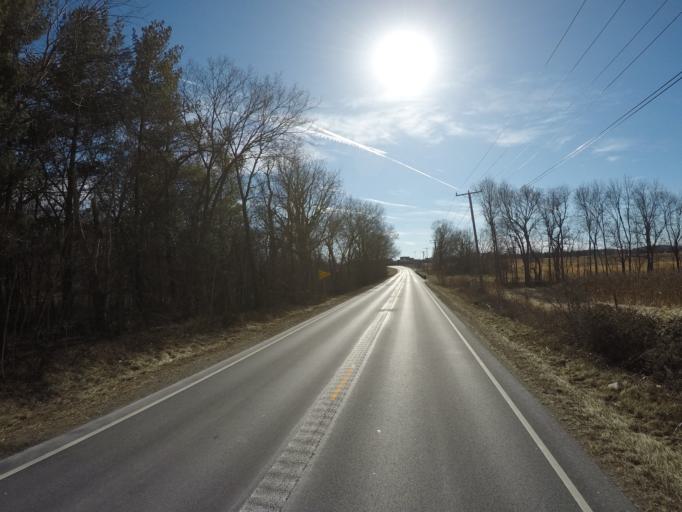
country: US
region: Virginia
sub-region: Loudoun County
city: Leesburg
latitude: 39.1787
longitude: -77.5364
